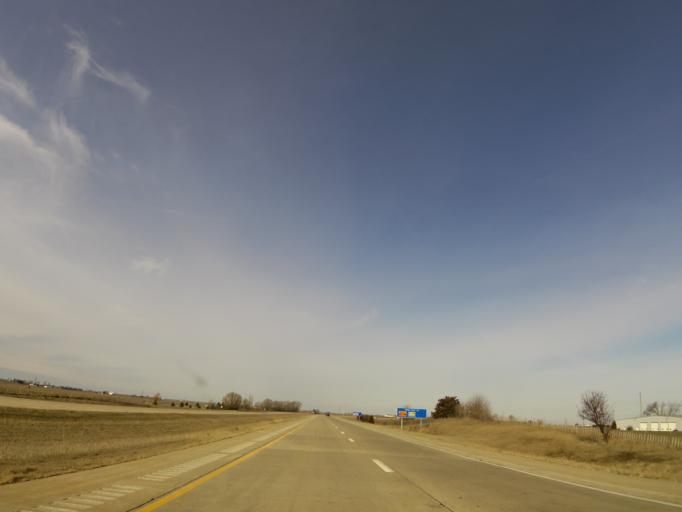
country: US
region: Illinois
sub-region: Woodford County
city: Minonk
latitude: 40.8925
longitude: -89.0449
